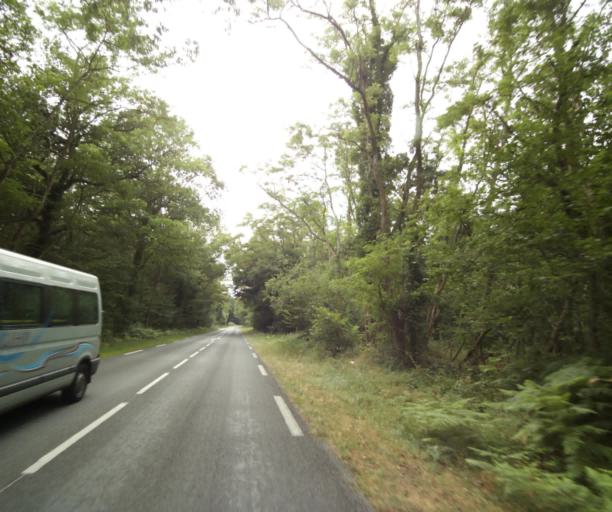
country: FR
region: Ile-de-France
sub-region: Departement de Seine-et-Marne
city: Arbonne-la-Foret
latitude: 48.4146
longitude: 2.5862
